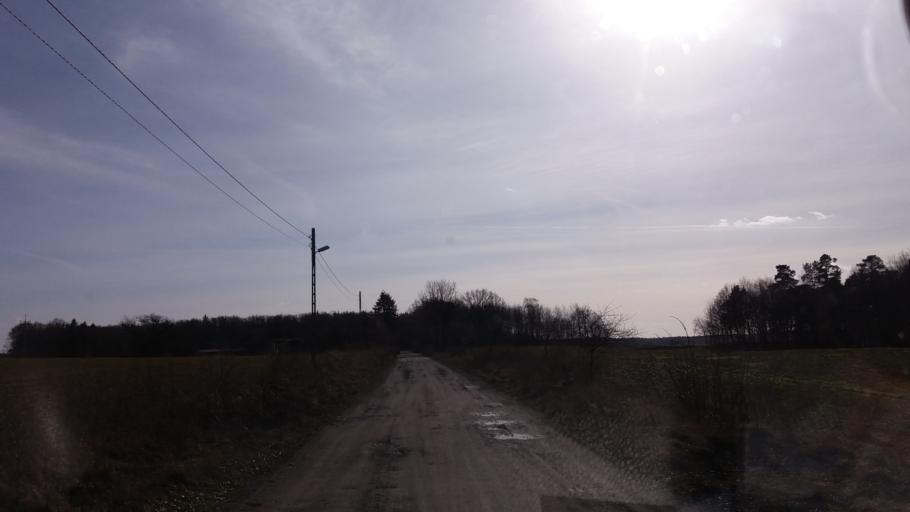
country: PL
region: West Pomeranian Voivodeship
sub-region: Powiat choszczenski
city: Pelczyce
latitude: 53.0061
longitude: 15.3698
